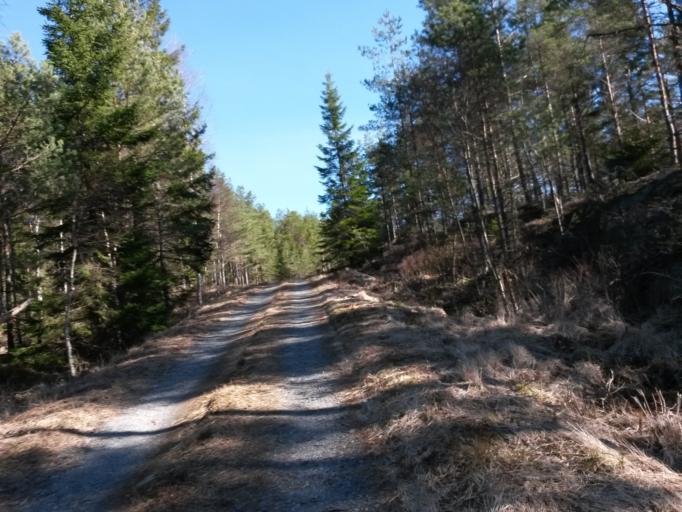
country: SE
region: Vaestra Goetaland
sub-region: Vargarda Kommun
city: Jonstorp
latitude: 57.9637
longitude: 12.6734
